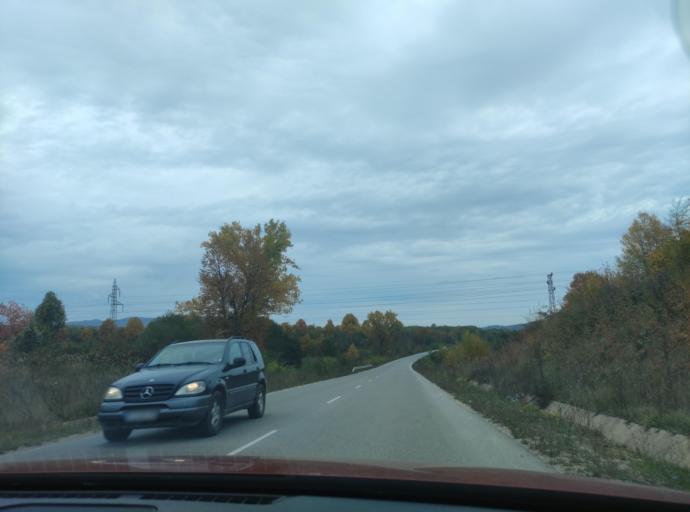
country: BG
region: Montana
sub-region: Obshtina Berkovitsa
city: Berkovitsa
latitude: 43.2330
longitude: 23.1587
